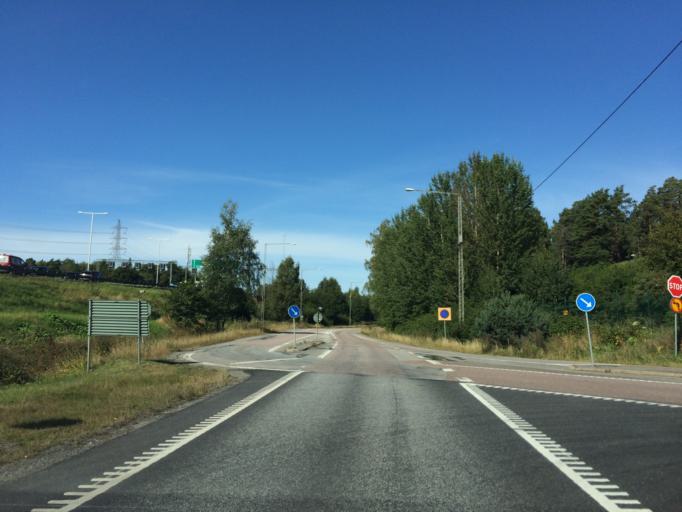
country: SE
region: Stockholm
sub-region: Solna Kommun
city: Rasunda
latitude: 59.3929
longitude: 17.9901
